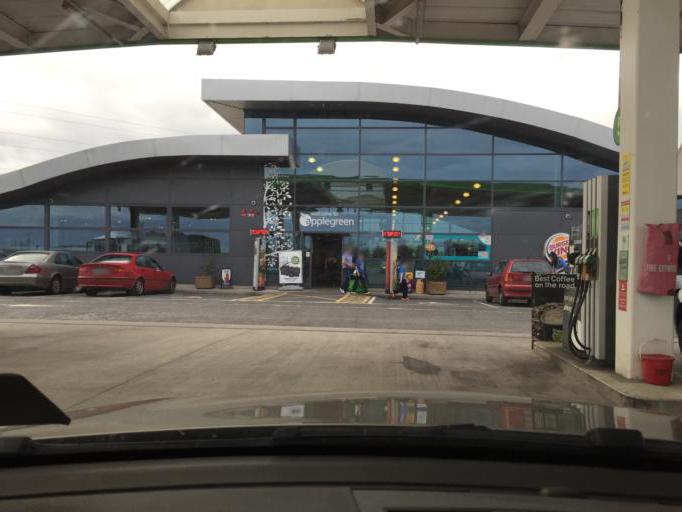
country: IE
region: Leinster
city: Lusk
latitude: 53.5405
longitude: -6.2097
